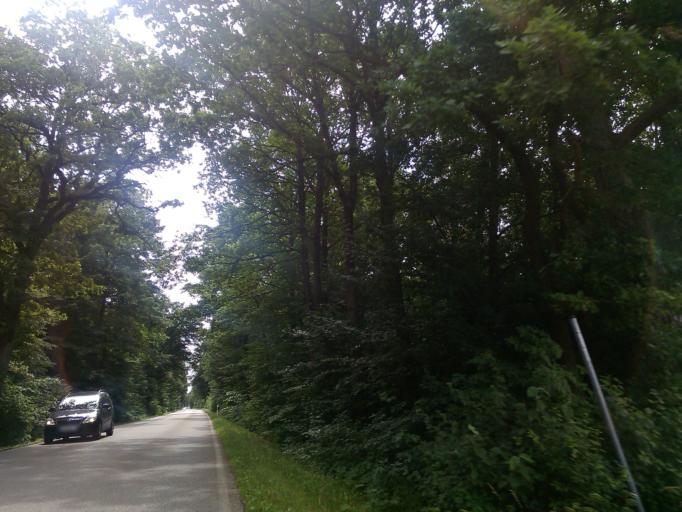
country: DE
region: Bavaria
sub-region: Upper Bavaria
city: Gauting
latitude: 48.0812
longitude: 11.3495
